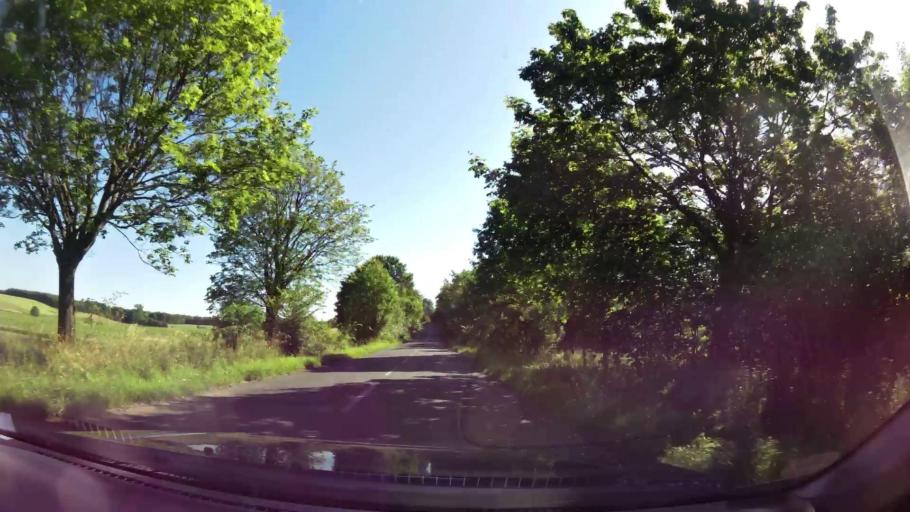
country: PL
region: West Pomeranian Voivodeship
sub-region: Powiat stargardzki
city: Dobrzany
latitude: 53.4167
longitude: 15.4217
